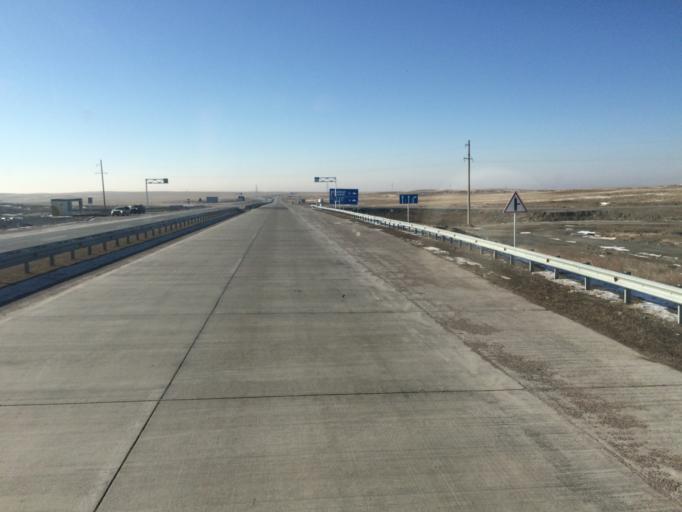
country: KZ
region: Zhambyl
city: Georgiyevka
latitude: 43.3531
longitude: 74.5593
